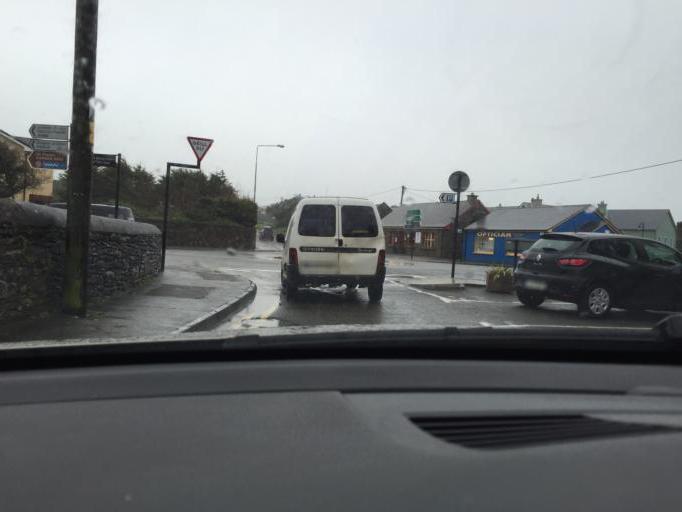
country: IE
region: Munster
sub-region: Ciarrai
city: Dingle
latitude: 52.1390
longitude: -10.2707
